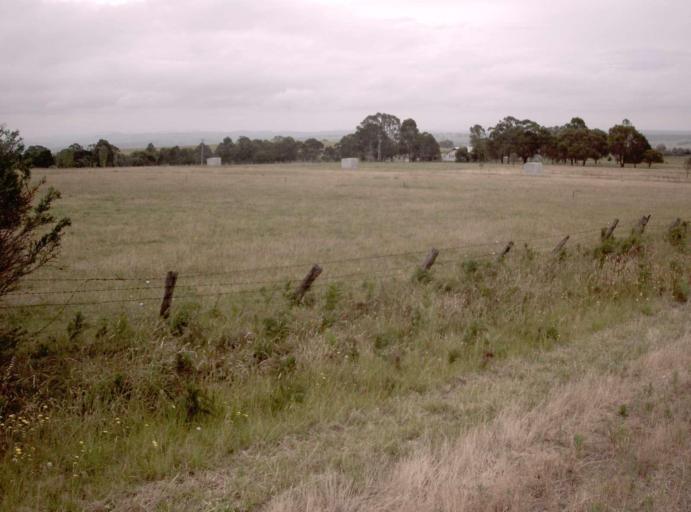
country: AU
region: Victoria
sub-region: East Gippsland
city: Bairnsdale
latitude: -37.8096
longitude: 147.4377
